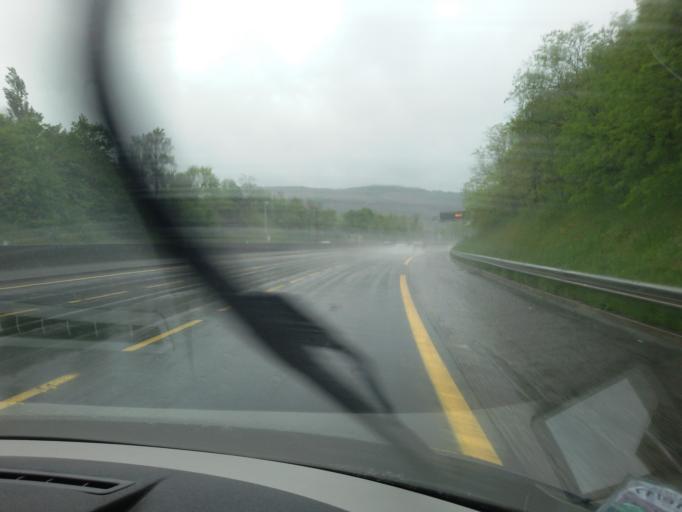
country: FR
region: Rhone-Alpes
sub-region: Departement du Rhone
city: Ampuis
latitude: 45.4888
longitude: 4.8329
